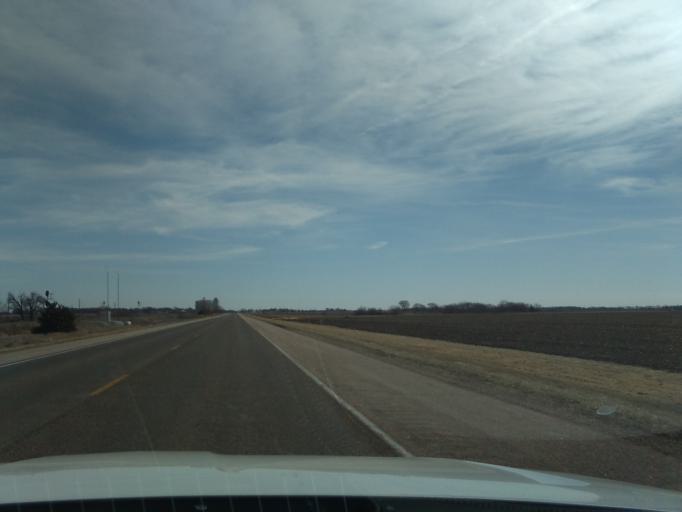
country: US
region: Nebraska
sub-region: Saline County
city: Friend
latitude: 40.6515
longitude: -97.1453
